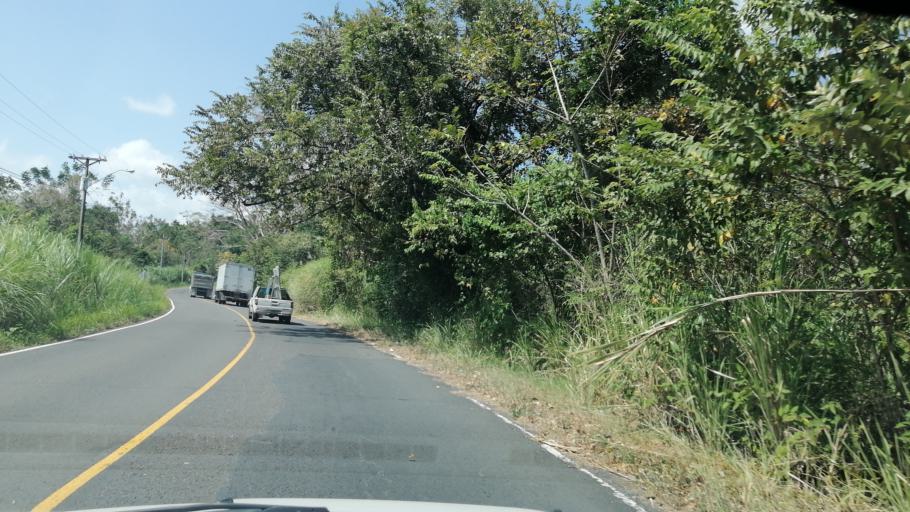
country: PA
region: Panama
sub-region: Distrito de Panama
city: Ancon
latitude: 8.9295
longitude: -79.5706
